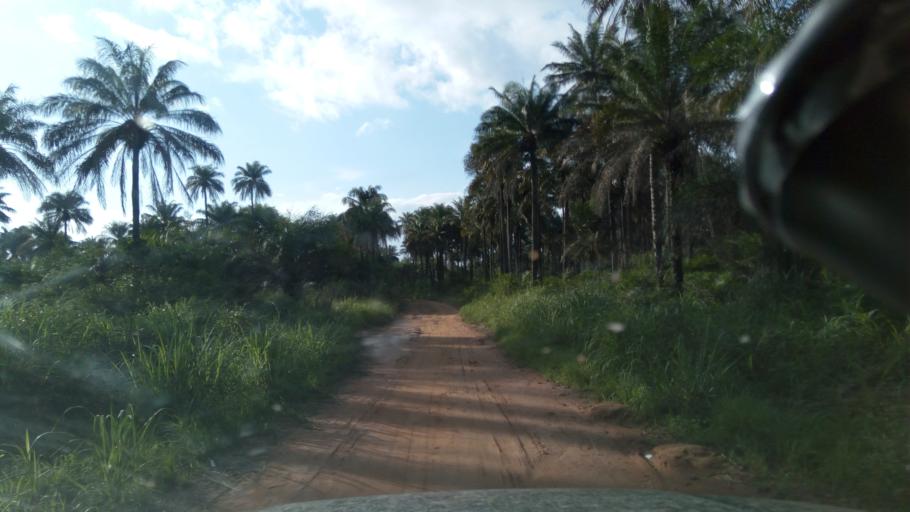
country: SL
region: Northern Province
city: Sawkta
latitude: 8.7035
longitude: -13.1170
